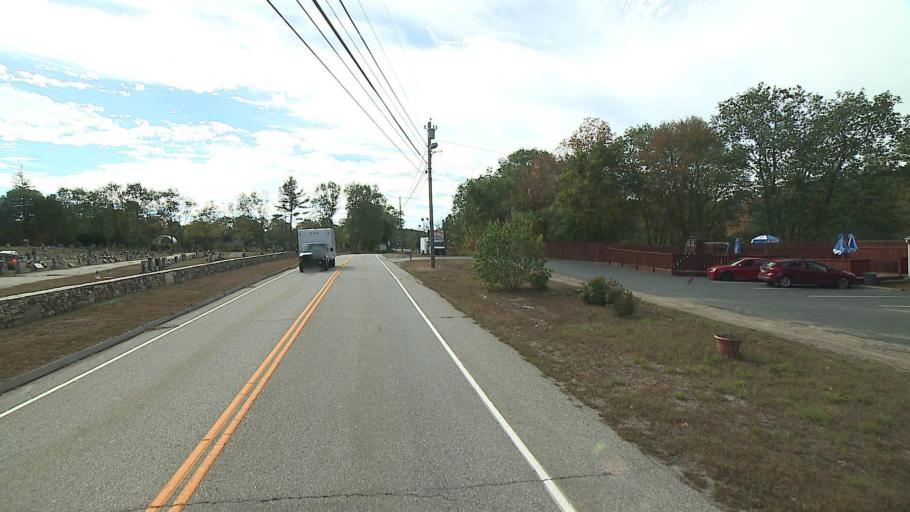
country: US
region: Connecticut
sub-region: Windham County
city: Thompson
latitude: 41.9502
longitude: -71.8870
